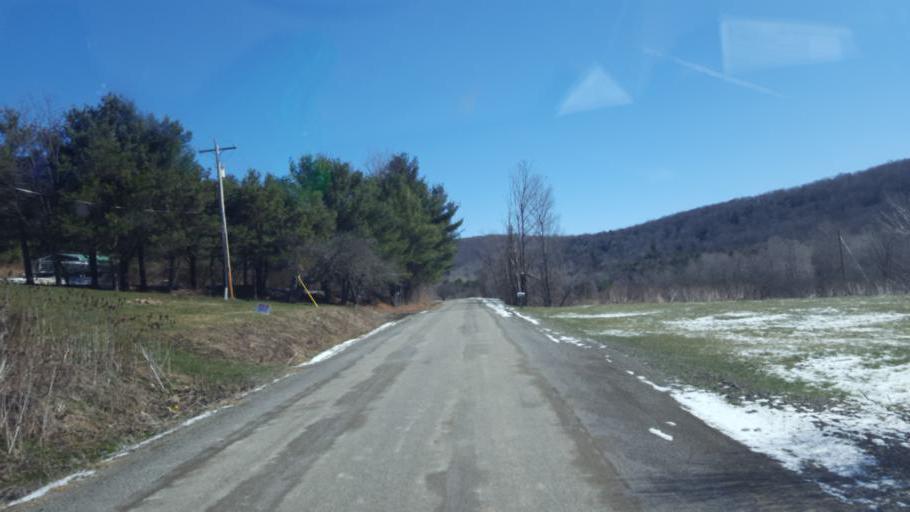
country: US
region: New York
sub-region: Allegany County
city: Wellsville
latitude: 42.0503
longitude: -77.9621
